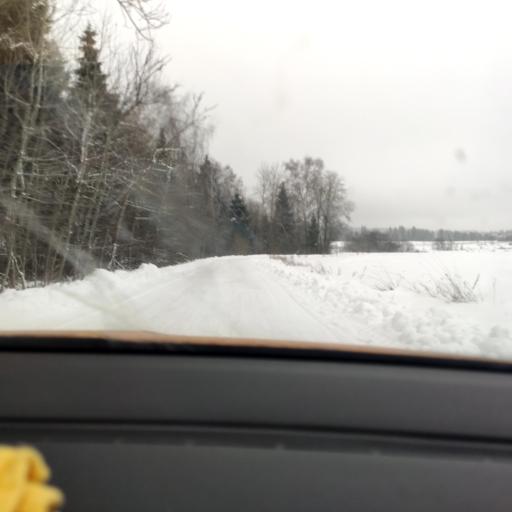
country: RU
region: Moskovskaya
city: Yershovo
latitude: 55.7884
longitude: 36.7818
